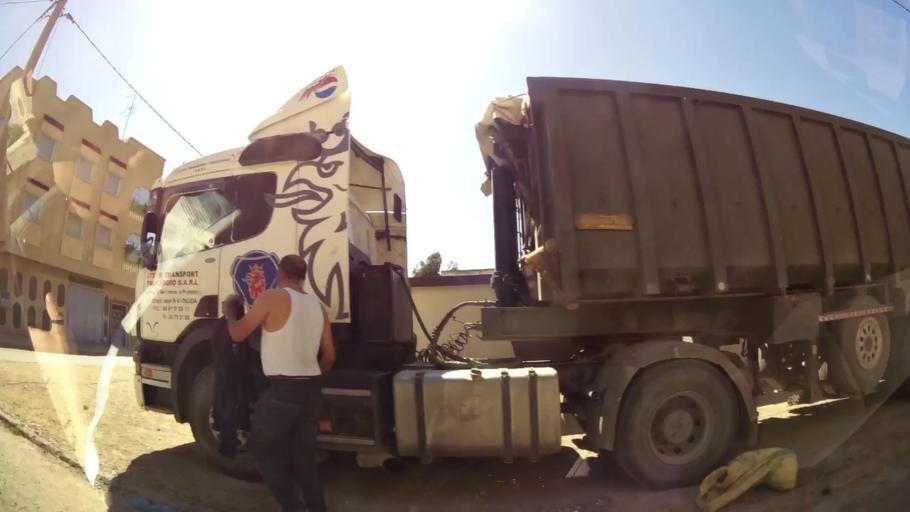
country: MA
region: Oriental
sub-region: Oujda-Angad
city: Oujda
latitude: 34.6852
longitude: -1.9381
